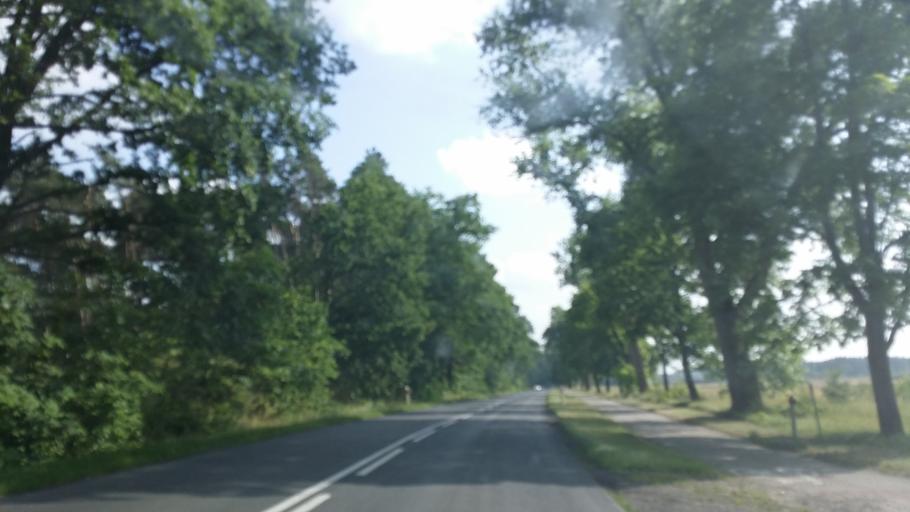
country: PL
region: Lubusz
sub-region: Powiat gorzowski
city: Klodawa
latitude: 52.8008
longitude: 15.2187
